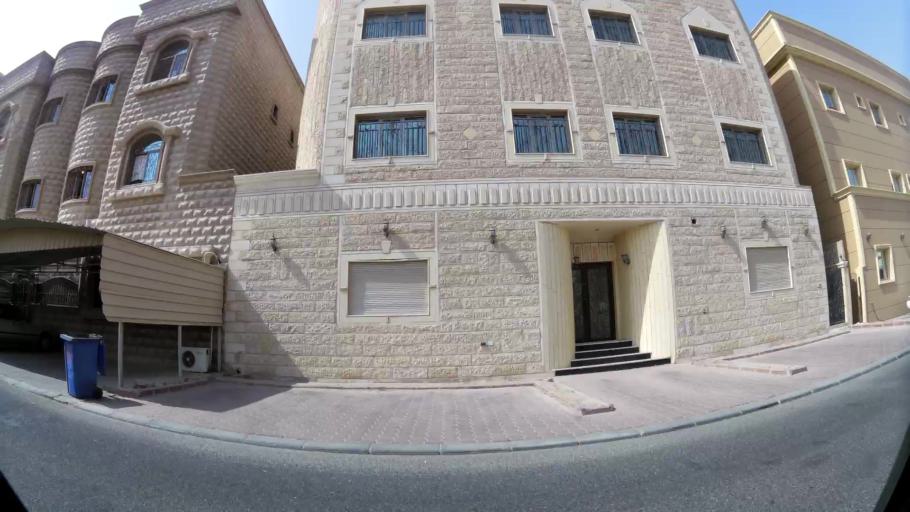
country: KW
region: Muhafazat al Jahra'
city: Al Jahra'
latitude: 29.3040
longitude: 47.7064
